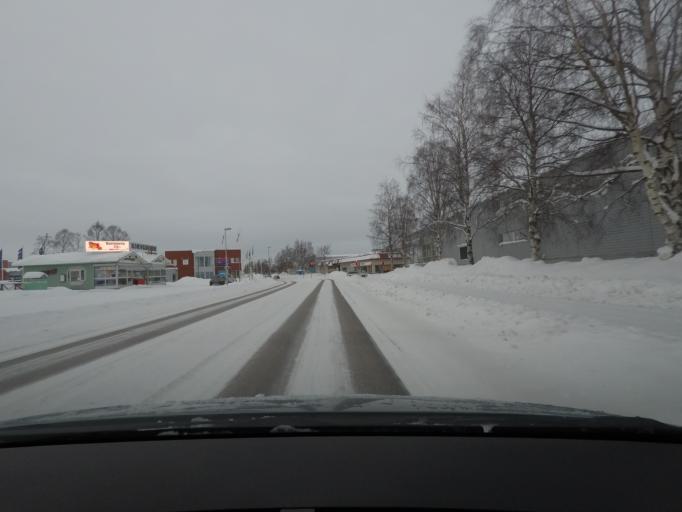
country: SE
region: Norrbotten
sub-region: Lulea Kommun
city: Lulea
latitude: 65.5987
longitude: 22.1444
